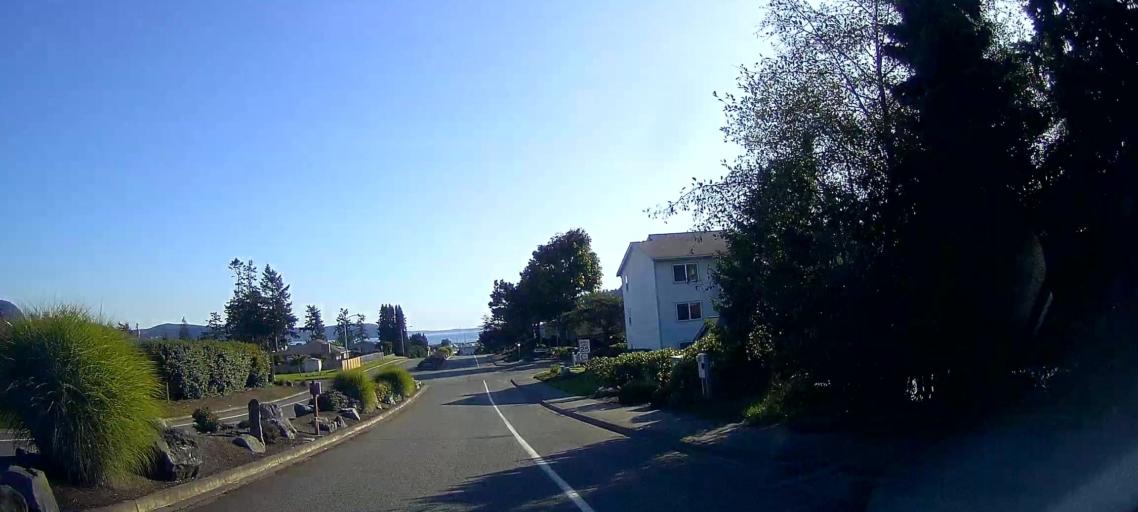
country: US
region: Washington
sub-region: Skagit County
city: Anacortes
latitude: 48.4981
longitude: -122.6856
